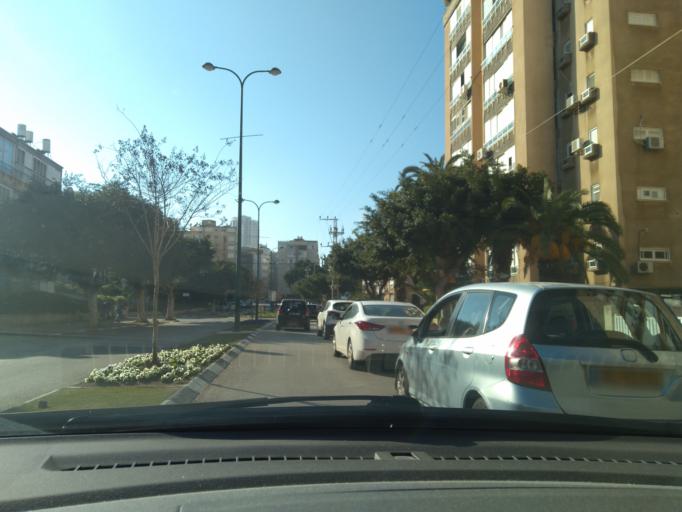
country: IL
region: Central District
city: Netanya
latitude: 32.3318
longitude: 34.8585
